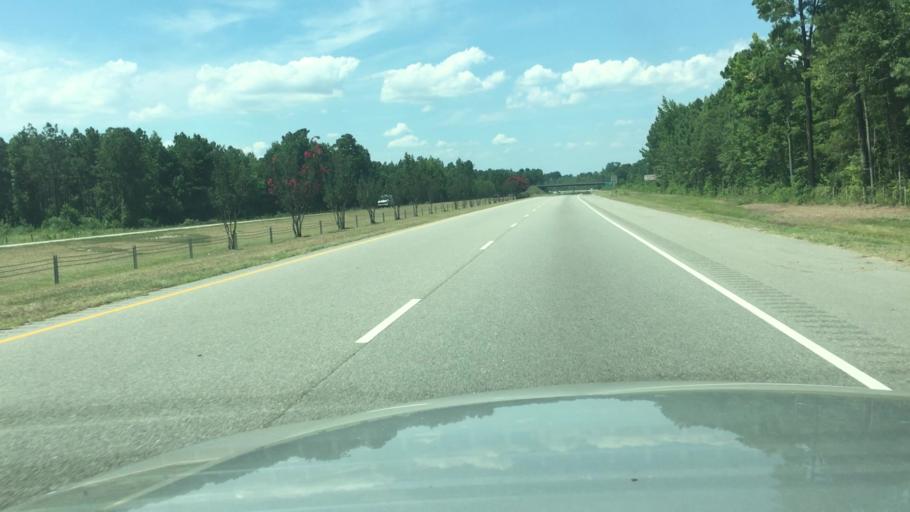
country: US
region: North Carolina
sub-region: Cumberland County
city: Fayetteville
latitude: 35.0173
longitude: -78.8709
